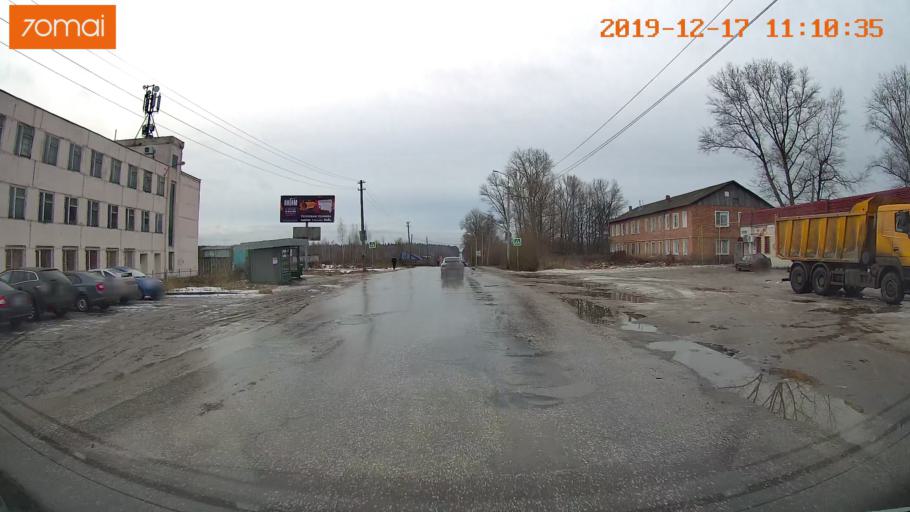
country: RU
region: Vladimir
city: Gus'-Khrustal'nyy
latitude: 55.5917
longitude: 40.6407
